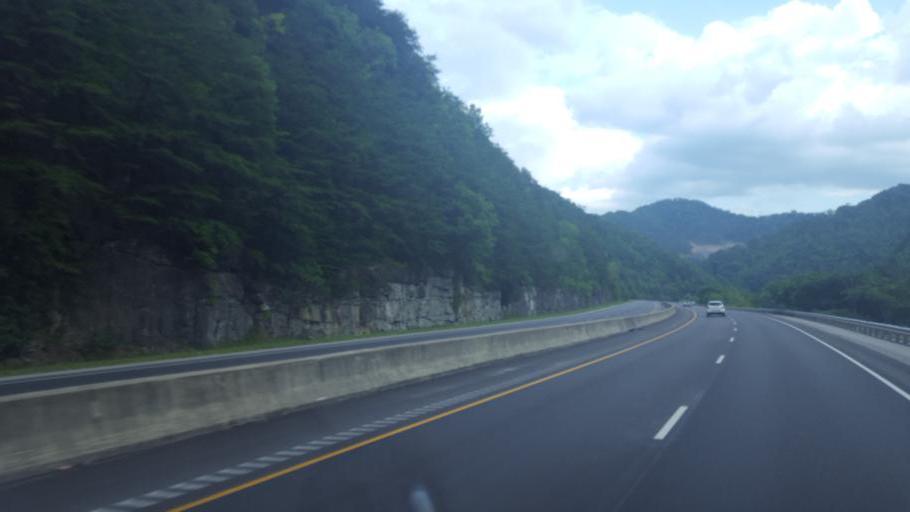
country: US
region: Kentucky
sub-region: Pike County
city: Pikeville
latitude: 37.3521
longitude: -82.5533
